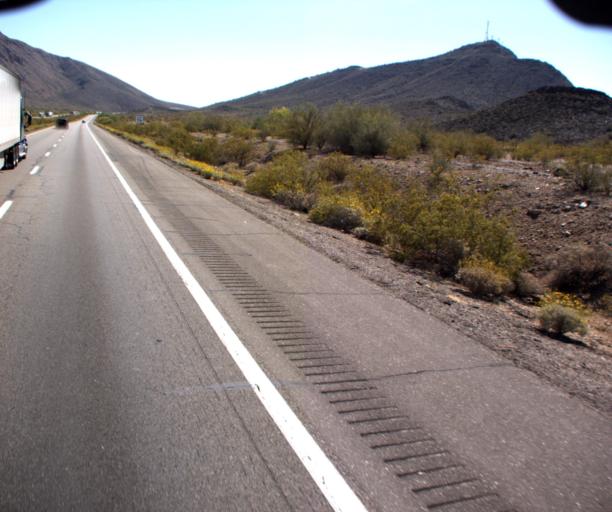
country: US
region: Arizona
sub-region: La Paz County
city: Quartzsite
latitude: 33.6788
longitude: -114.0757
